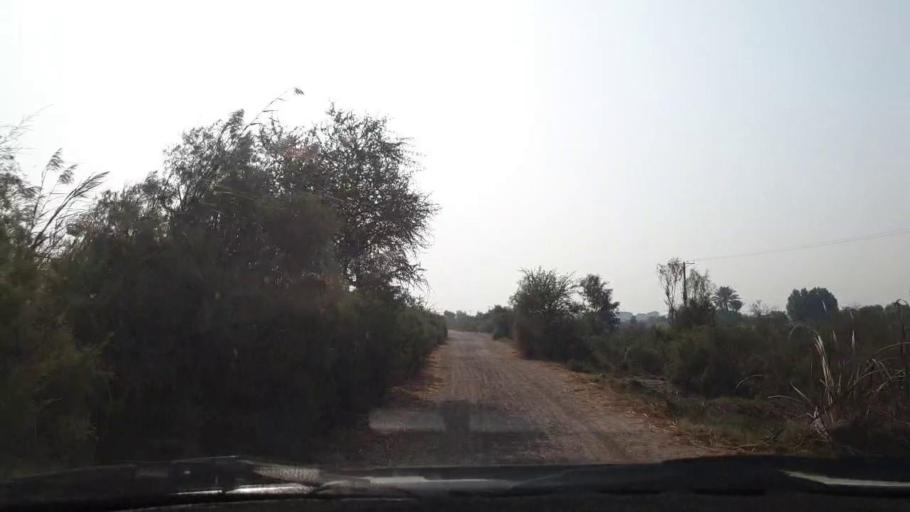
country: PK
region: Sindh
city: Tando Muhammad Khan
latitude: 25.0172
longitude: 68.4505
